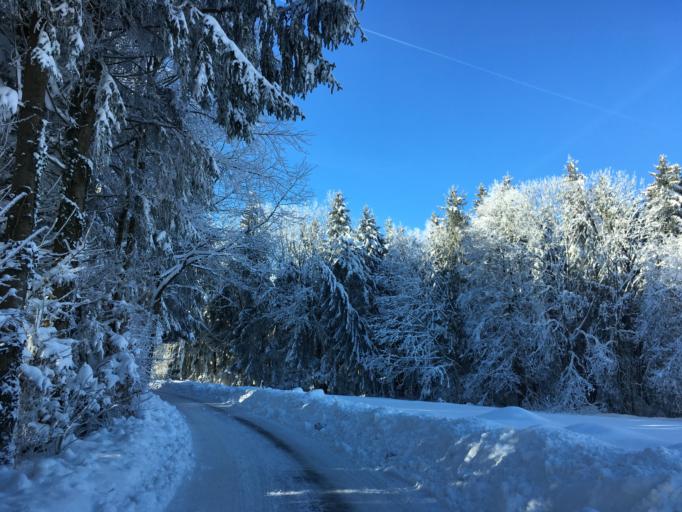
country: DE
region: Bavaria
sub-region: Upper Bavaria
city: Bad Endorf
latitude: 47.8782
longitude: 12.3049
